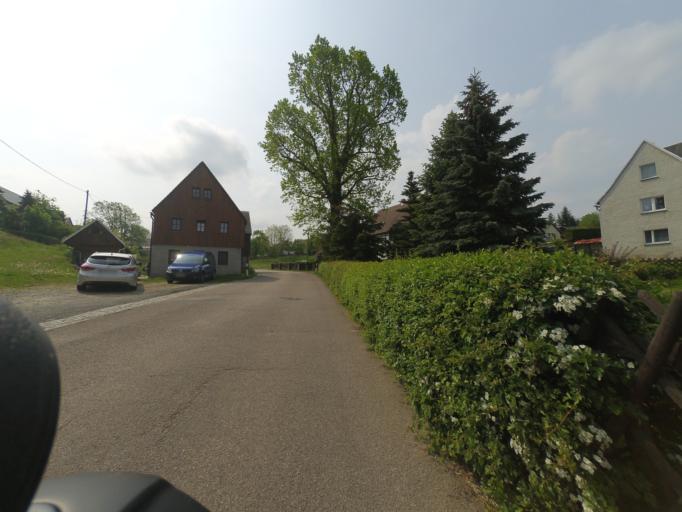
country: DE
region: Saxony
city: Obercunnersdorf
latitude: 50.8880
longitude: 13.5831
